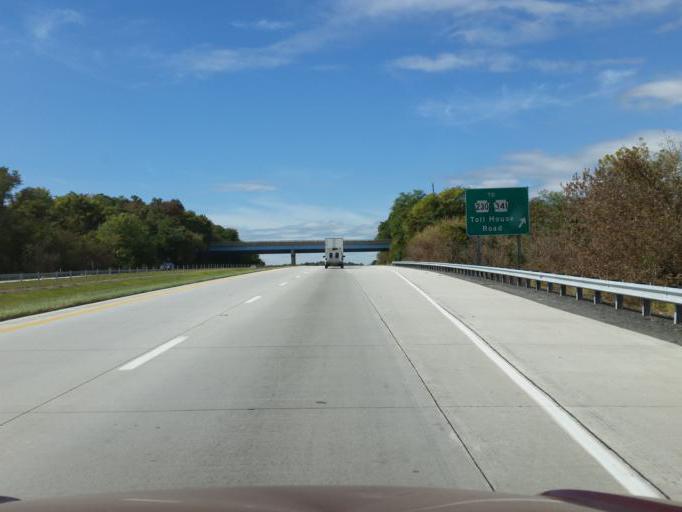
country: US
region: Pennsylvania
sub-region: Dauphin County
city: Middletown
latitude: 40.1944
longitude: -76.6740
